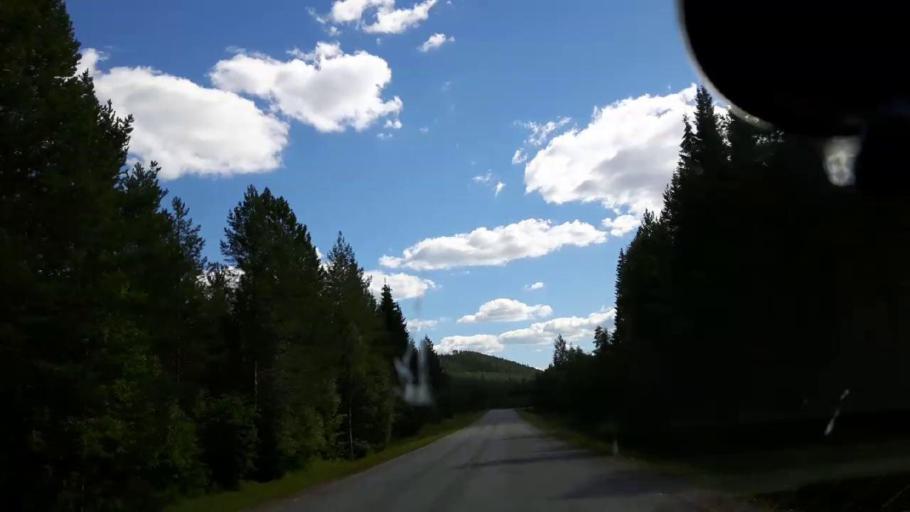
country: SE
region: Jaemtland
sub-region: Ragunda Kommun
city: Hammarstrand
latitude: 62.9514
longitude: 16.2120
